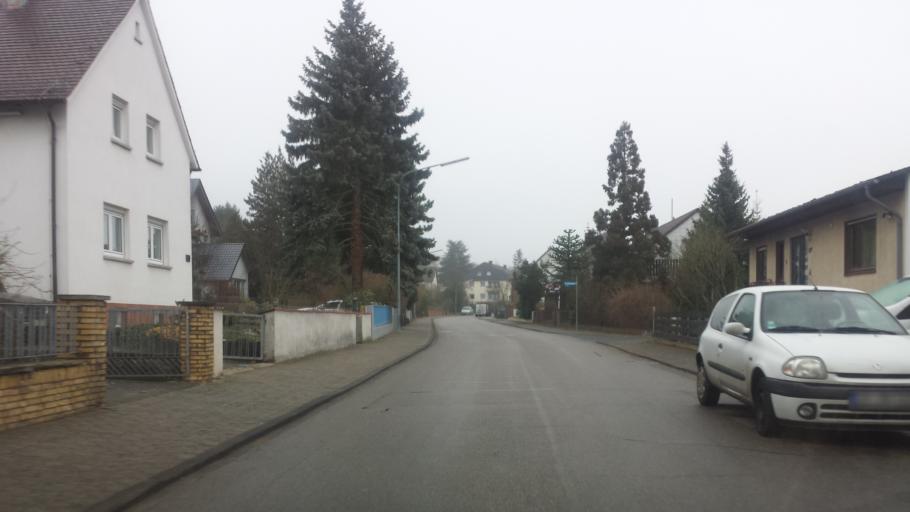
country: DE
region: Hesse
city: Ober-Ramstadt
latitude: 49.8407
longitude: 8.7049
